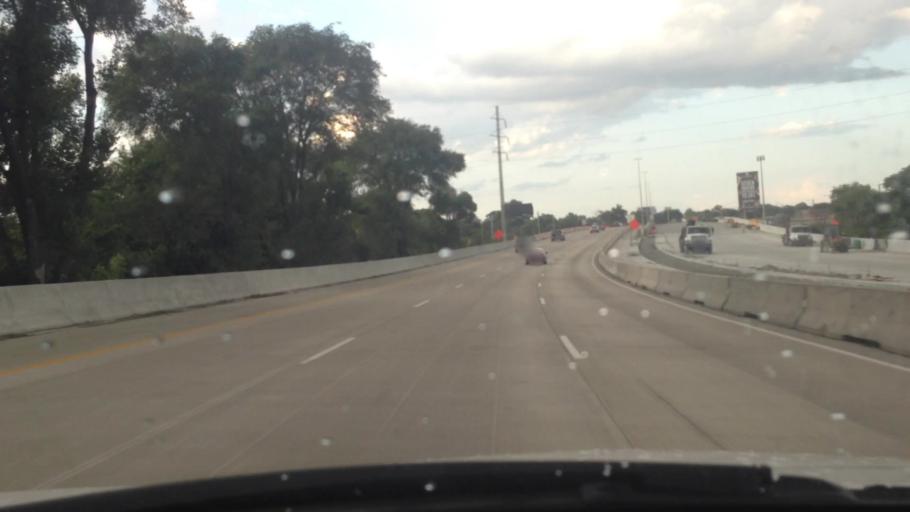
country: US
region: Michigan
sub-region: Wayne County
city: River Rouge
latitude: 42.2963
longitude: -83.1260
